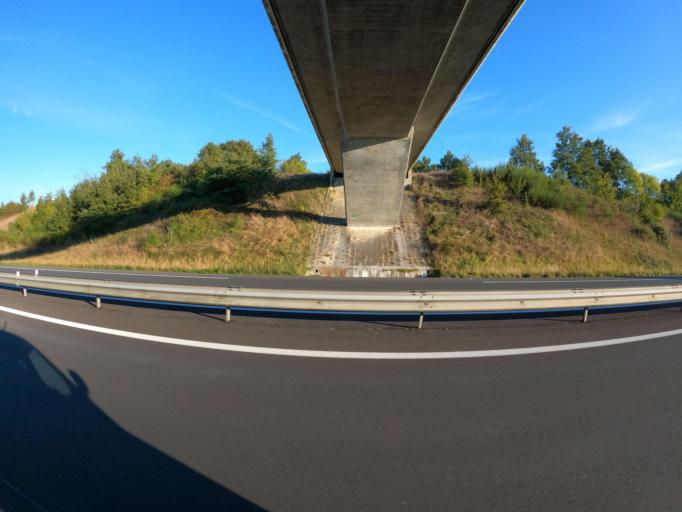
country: FR
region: Pays de la Loire
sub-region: Departement de la Vendee
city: Saint-Fulgent
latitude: 46.8294
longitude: -1.1690
